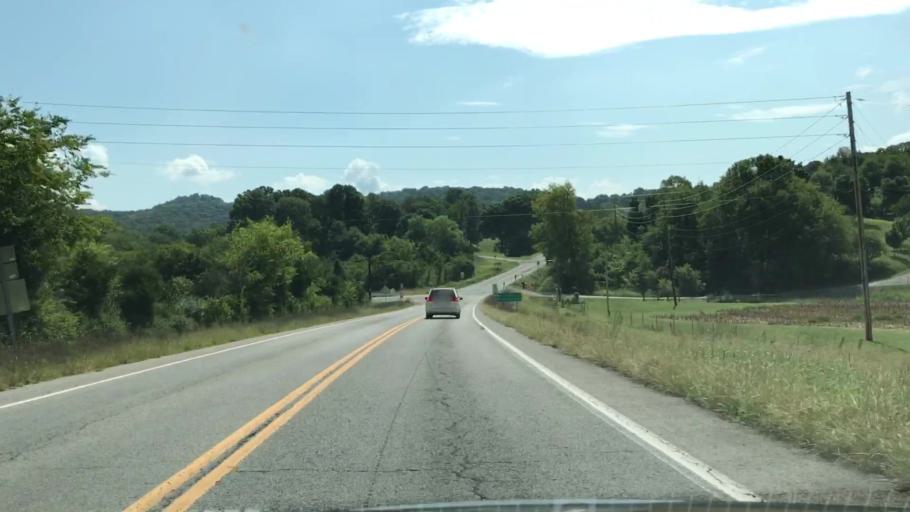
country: US
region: Tennessee
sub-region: Trousdale County
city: Hartsville
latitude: 36.3832
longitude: -86.1193
